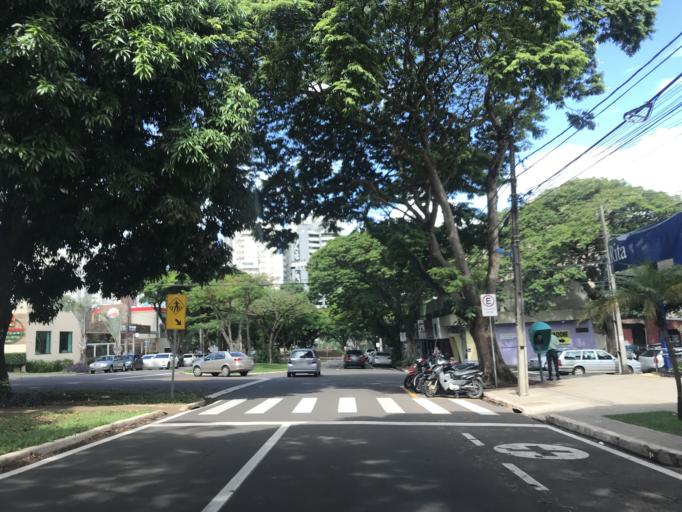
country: BR
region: Parana
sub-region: Maringa
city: Maringa
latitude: -23.4261
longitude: -51.9501
